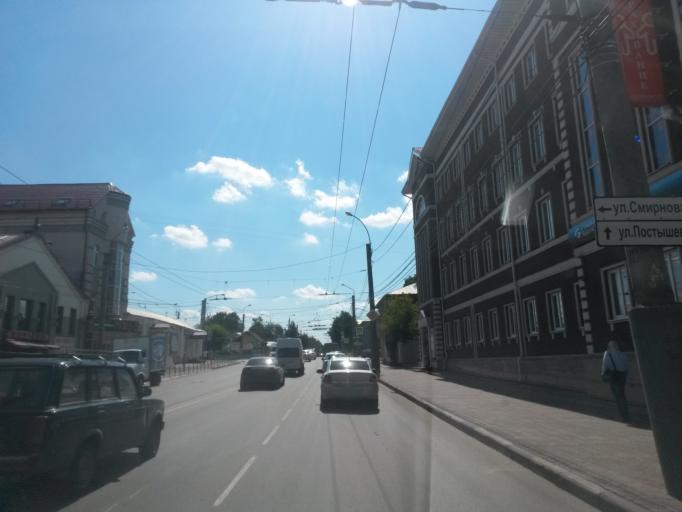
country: RU
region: Ivanovo
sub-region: Gorod Ivanovo
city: Ivanovo
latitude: 56.9934
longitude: 40.9866
